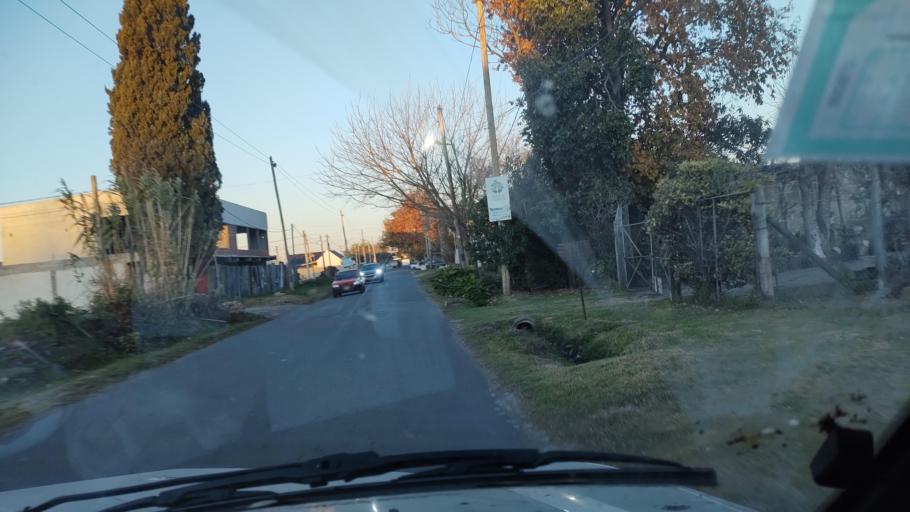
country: AR
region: Buenos Aires
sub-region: Partido de La Plata
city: La Plata
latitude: -34.9063
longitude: -58.0358
